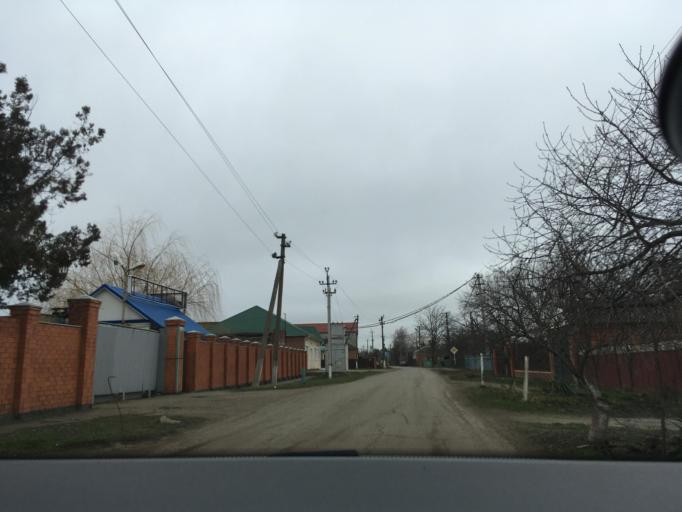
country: RU
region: Krasnodarskiy
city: Kushchevskaya
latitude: 46.5749
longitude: 39.6236
